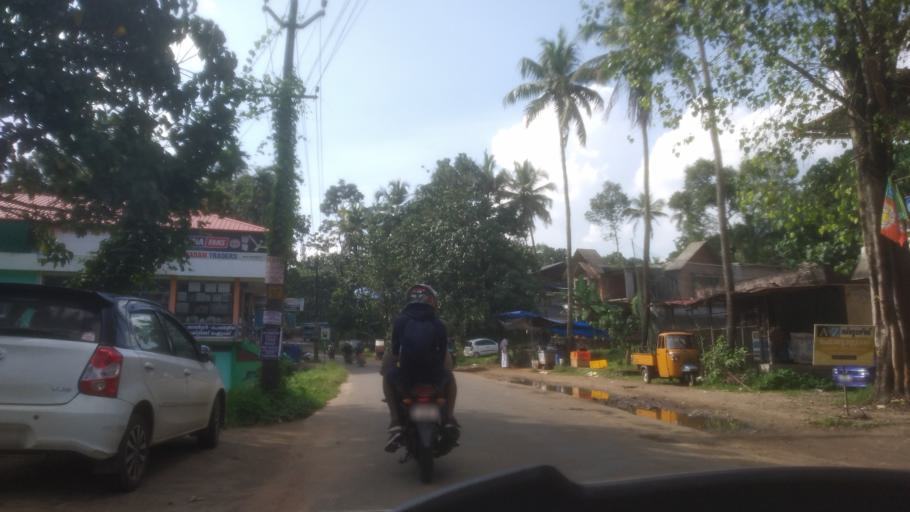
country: IN
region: Kerala
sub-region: Ernakulam
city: Muvattupula
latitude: 9.9982
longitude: 76.6366
